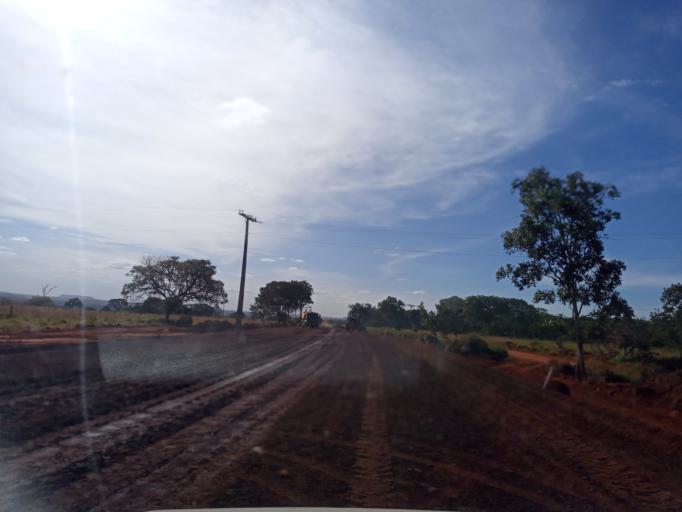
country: BR
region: Minas Gerais
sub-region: Ituiutaba
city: Ituiutaba
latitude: -18.9752
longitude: -49.5047
